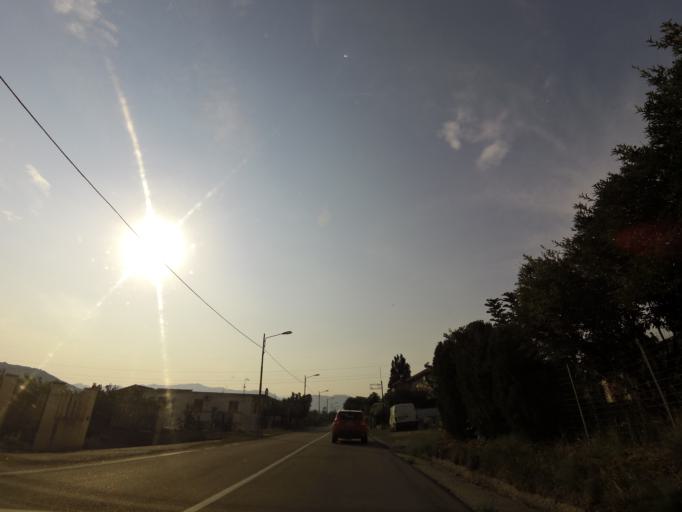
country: IT
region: Calabria
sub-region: Provincia di Reggio Calabria
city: Monasterace
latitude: 38.4442
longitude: 16.5385
